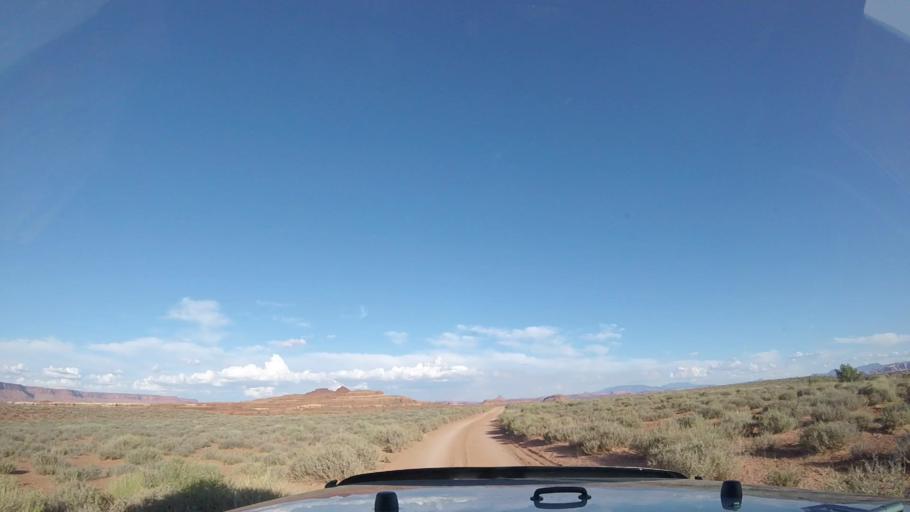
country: US
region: Utah
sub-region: Grand County
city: Moab
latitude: 38.2146
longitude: -109.7926
